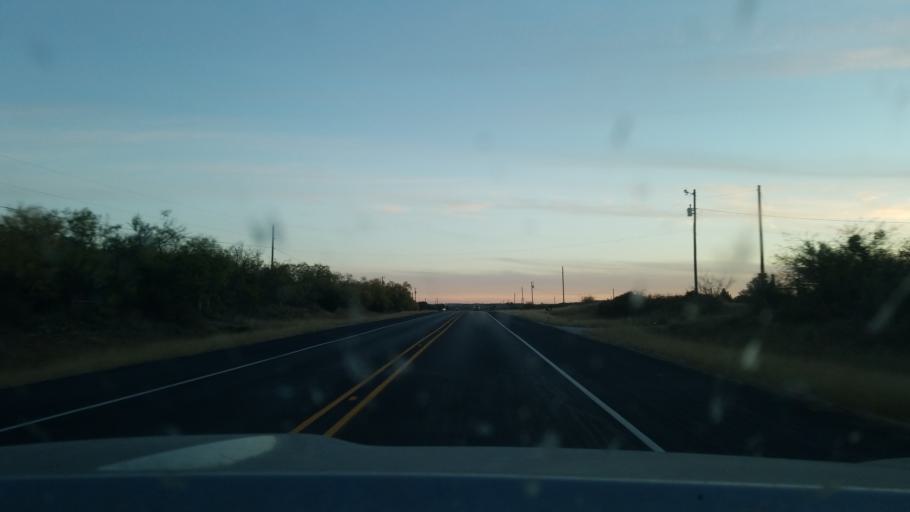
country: US
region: Texas
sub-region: Stephens County
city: Breckenridge
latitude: 32.6061
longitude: -98.8993
